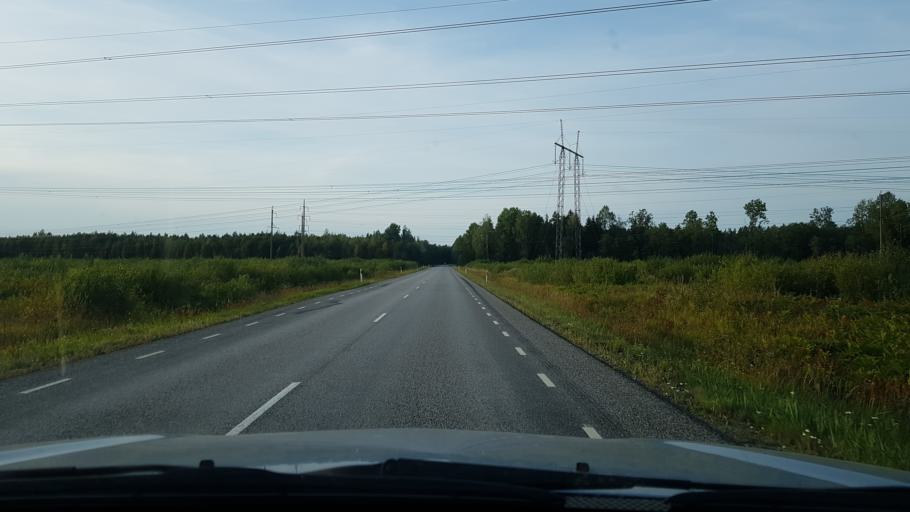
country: EE
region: Ida-Virumaa
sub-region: Narva-Joesuu linn
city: Narva-Joesuu
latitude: 59.3486
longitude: 27.9318
